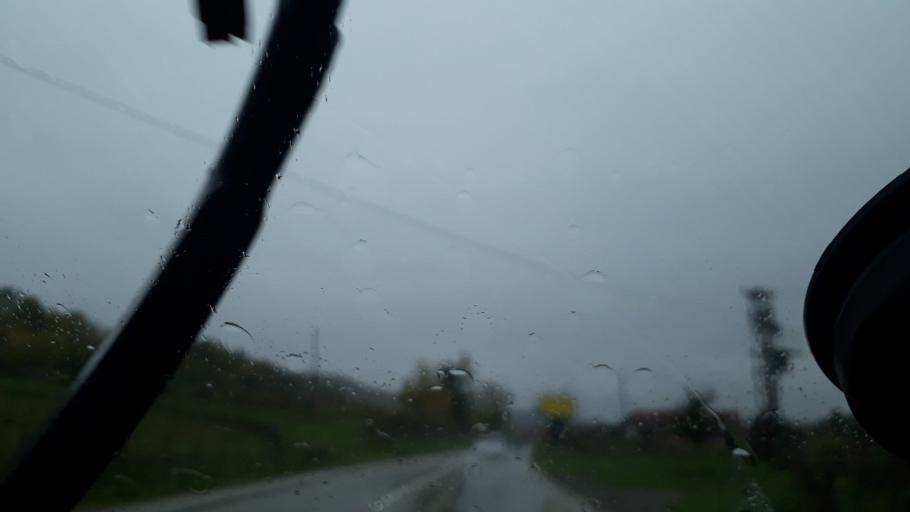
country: BA
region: Republika Srpska
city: Maglajani
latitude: 44.8662
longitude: 17.4264
